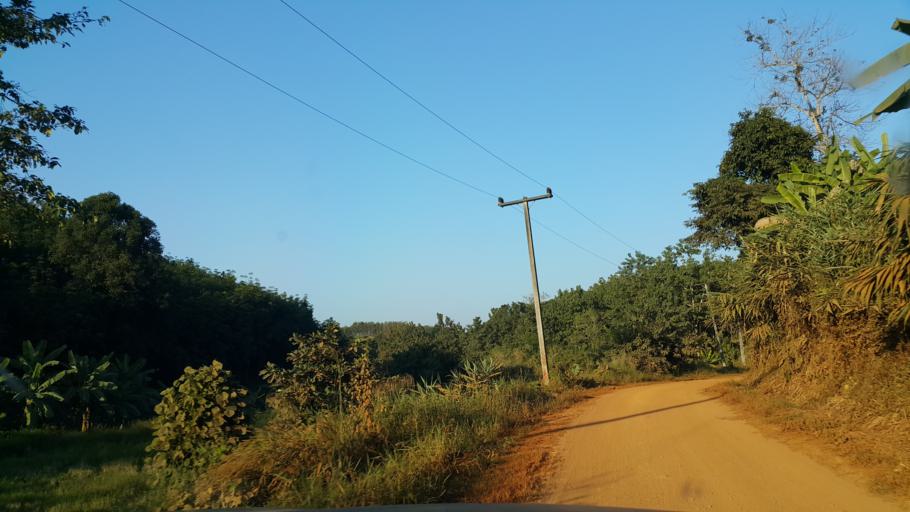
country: TH
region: Sukhothai
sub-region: Amphoe Si Satchanalai
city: Si Satchanalai
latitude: 17.6077
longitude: 99.6186
